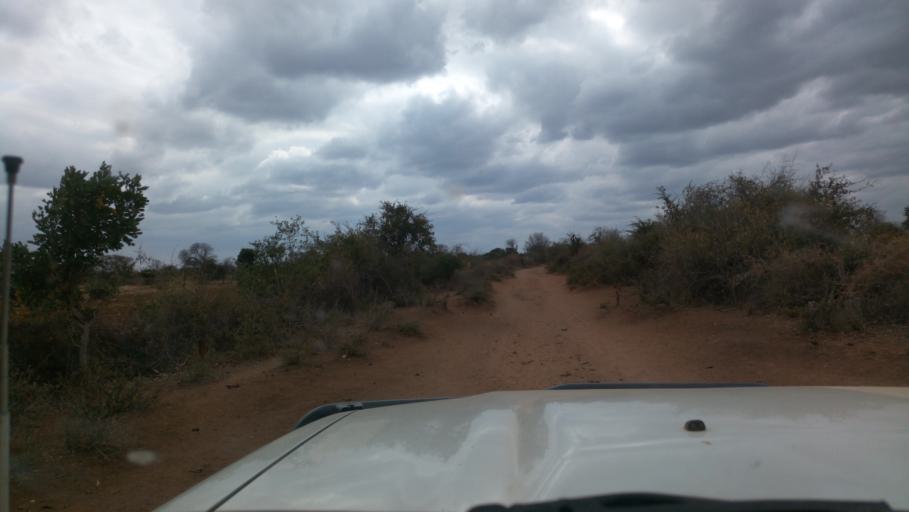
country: KE
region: Makueni
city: Mtito Andei
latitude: -2.0743
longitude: 38.2899
